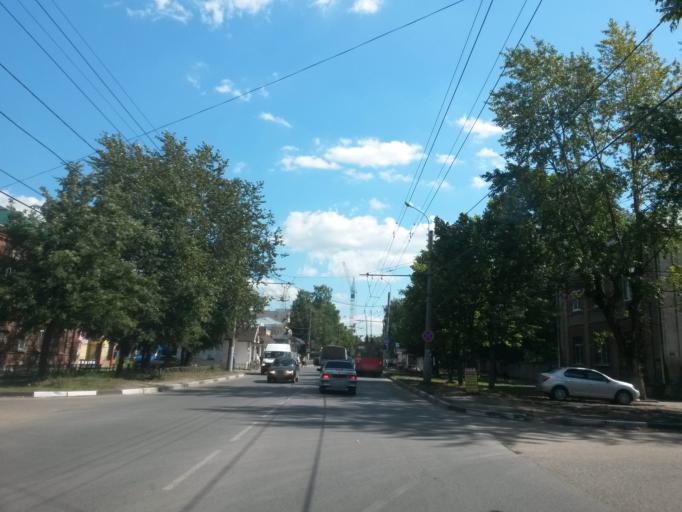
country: RU
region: Ivanovo
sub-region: Gorod Ivanovo
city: Ivanovo
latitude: 56.9860
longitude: 40.9908
